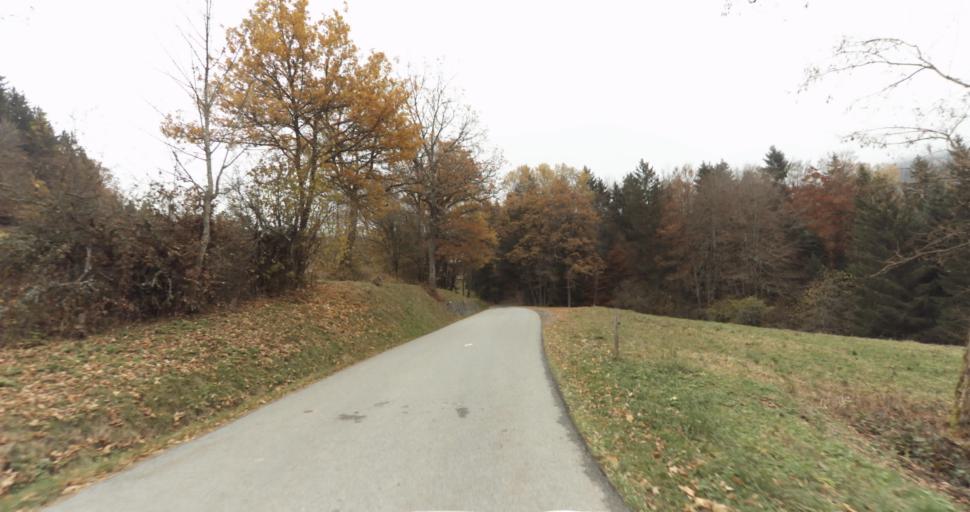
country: FR
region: Rhone-Alpes
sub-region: Departement de la Haute-Savoie
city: Saint-Jorioz
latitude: 45.7562
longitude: 6.1345
